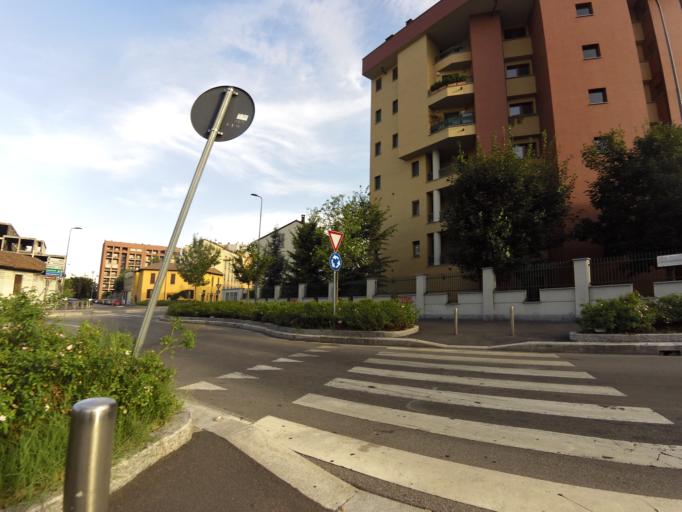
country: IT
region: Lombardy
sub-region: Citta metropolitana di Milano
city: Chiaravalle
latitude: 45.4368
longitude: 9.2346
